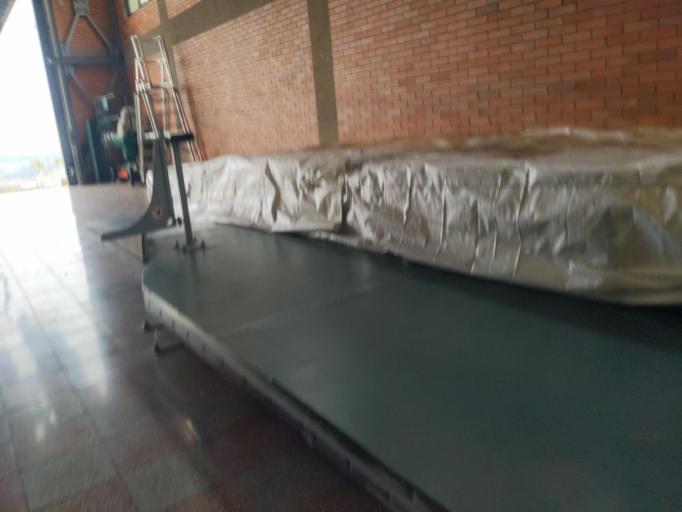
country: DE
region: Saxony-Anhalt
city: Thale
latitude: 51.7351
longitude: 11.0286
